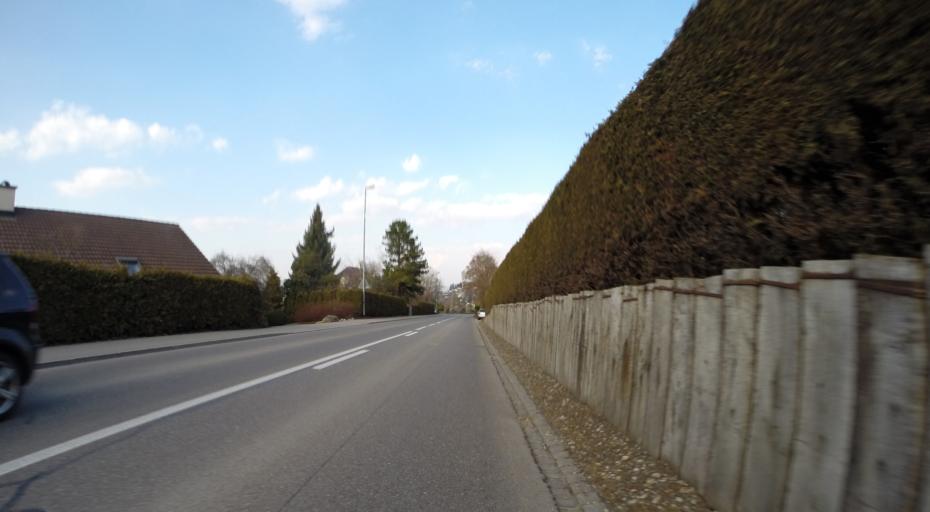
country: CH
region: Thurgau
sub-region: Frauenfeld District
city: Steckborn
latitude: 47.6606
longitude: 8.9817
